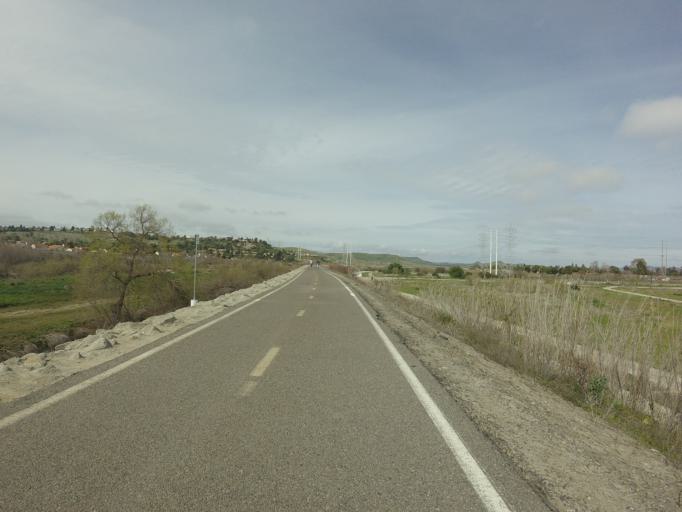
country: US
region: California
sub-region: San Diego County
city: Camp Pendleton South
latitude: 33.2253
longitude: -117.3431
